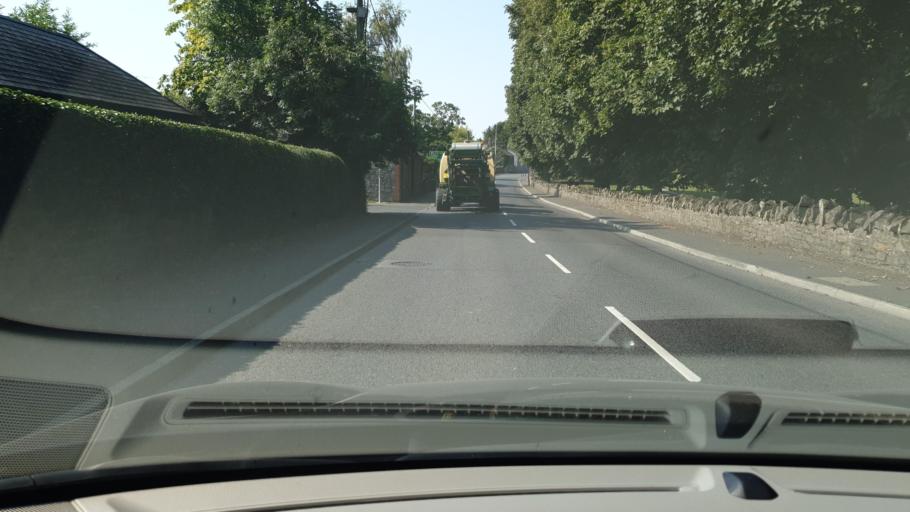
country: IE
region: Leinster
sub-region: An Mhi
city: Athboy
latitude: 53.6223
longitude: -6.9133
